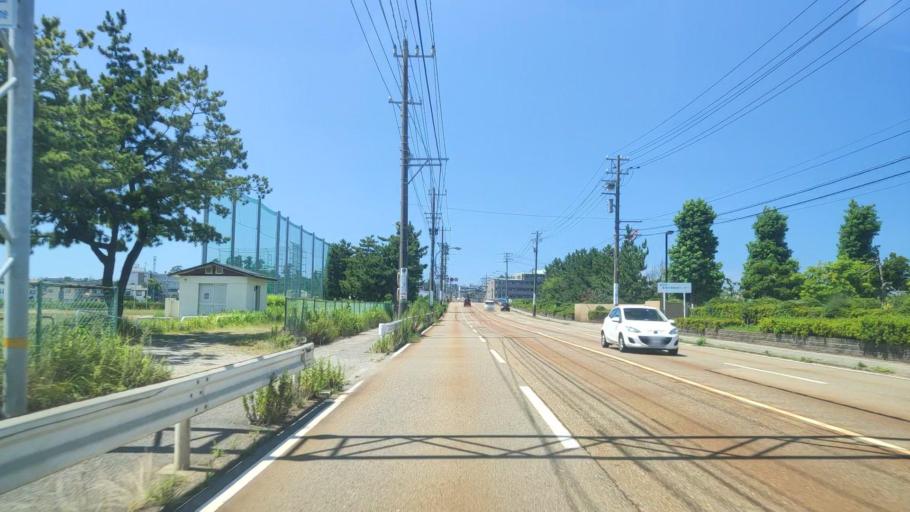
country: JP
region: Ishikawa
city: Kanazawa-shi
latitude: 36.6197
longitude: 136.6293
